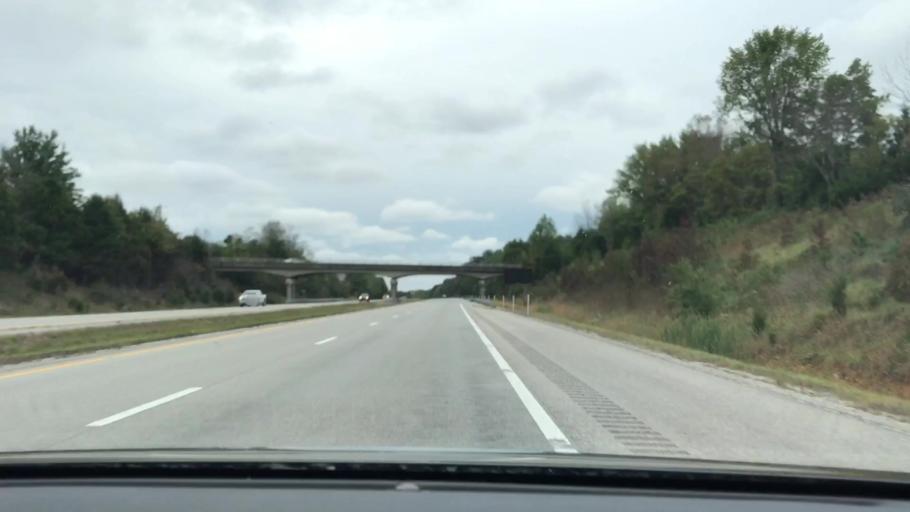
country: US
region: Kentucky
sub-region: Barren County
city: Cave City
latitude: 37.0369
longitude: -86.0587
